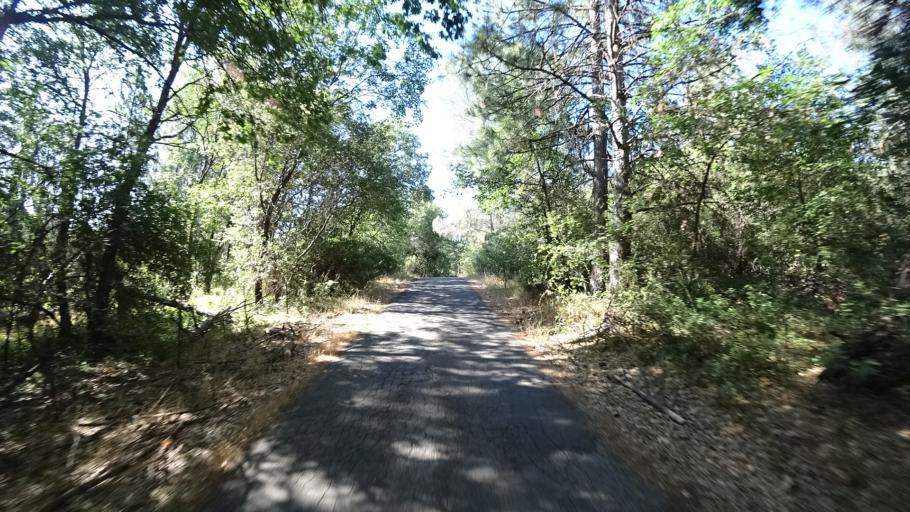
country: US
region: California
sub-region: Amador County
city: Pioneer
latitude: 38.4013
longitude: -120.5573
